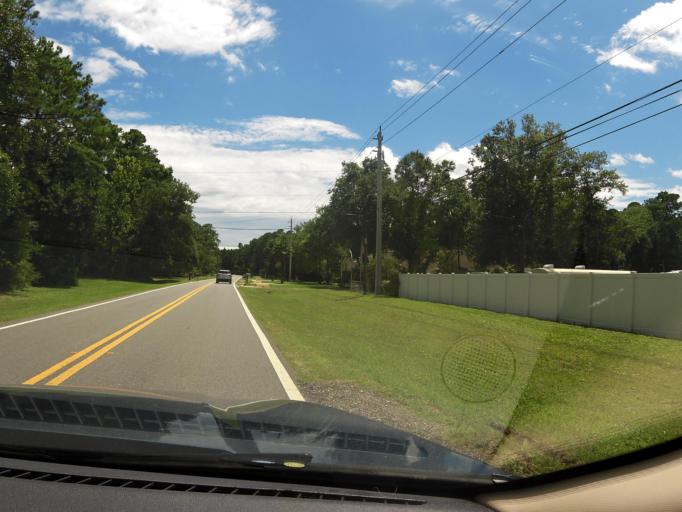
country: US
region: Florida
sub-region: Nassau County
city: Fernandina Beach
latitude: 30.6534
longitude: -81.5287
